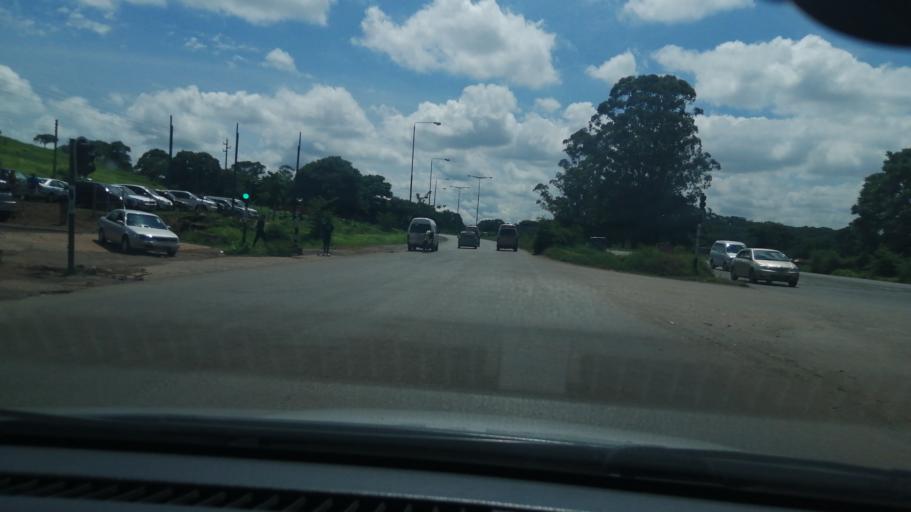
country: ZW
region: Harare
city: Harare
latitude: -17.8254
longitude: 30.9823
